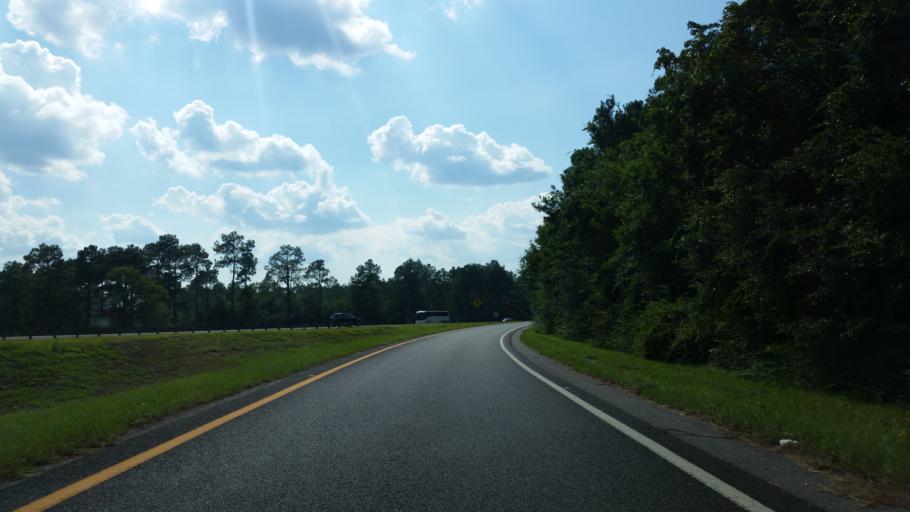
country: US
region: Florida
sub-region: Escambia County
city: Gonzalez
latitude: 30.5354
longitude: -87.3344
